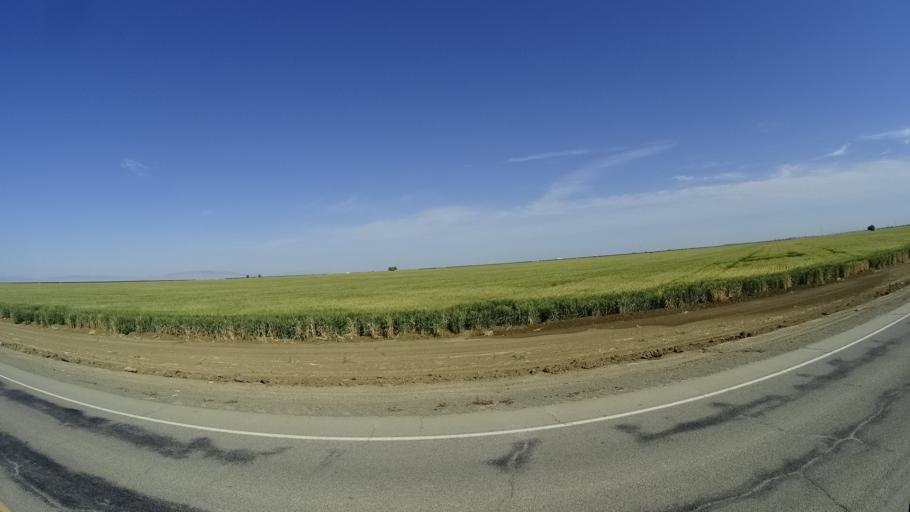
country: US
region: California
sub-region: Kings County
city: Lemoore Station
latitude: 36.2055
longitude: -119.9248
